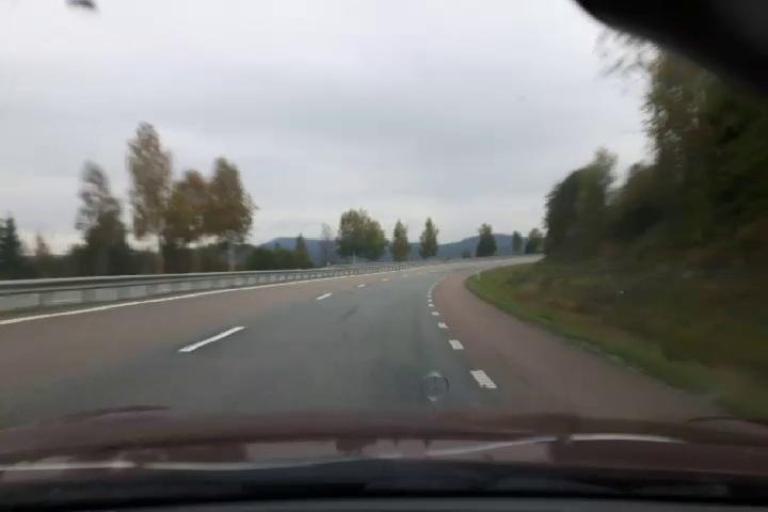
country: SE
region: Vaesternorrland
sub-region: Kramfors Kommun
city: Nordingra
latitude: 63.0073
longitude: 18.2840
